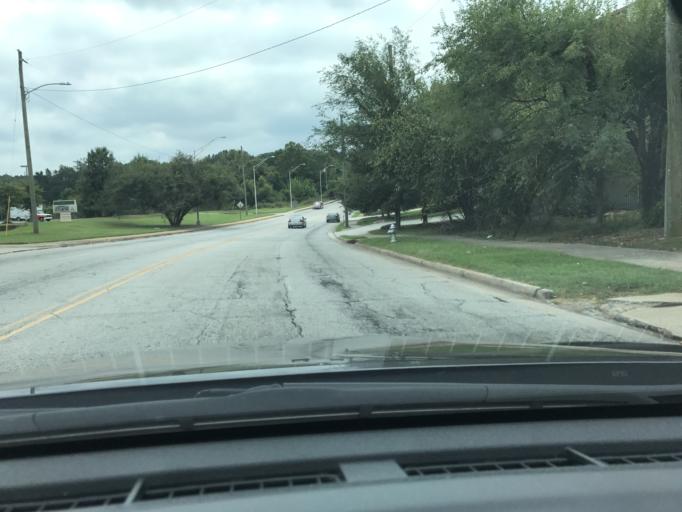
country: US
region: Georgia
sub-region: DeKalb County
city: Druid Hills
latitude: 33.7471
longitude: -84.3333
